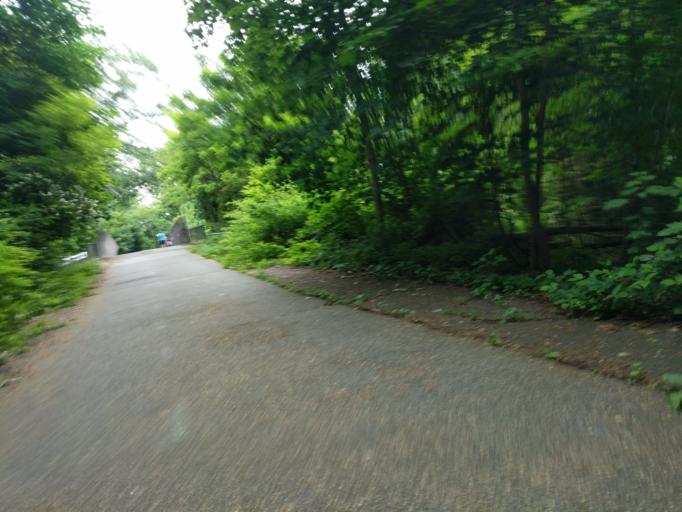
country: US
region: New York
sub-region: Nassau County
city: Bellerose Terrace
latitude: 40.7364
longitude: -73.7574
